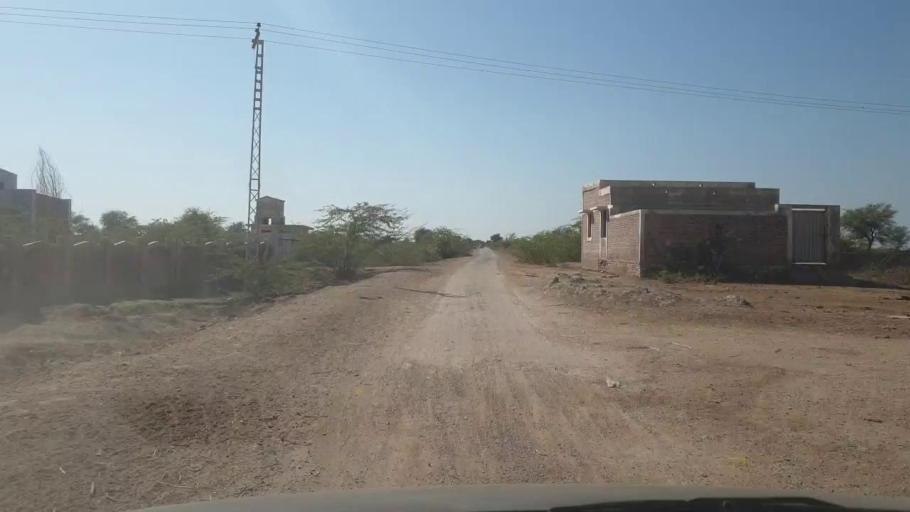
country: PK
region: Sindh
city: Dhoro Naro
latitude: 25.4008
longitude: 69.5915
